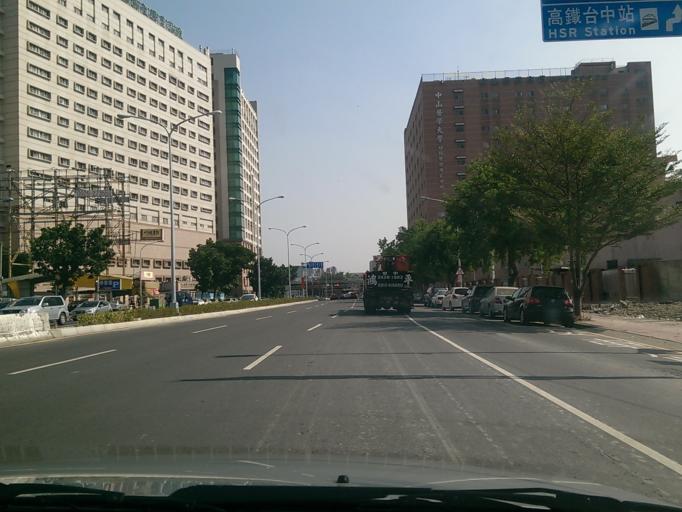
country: TW
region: Taiwan
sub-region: Taichung City
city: Taichung
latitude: 24.1225
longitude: 120.6486
